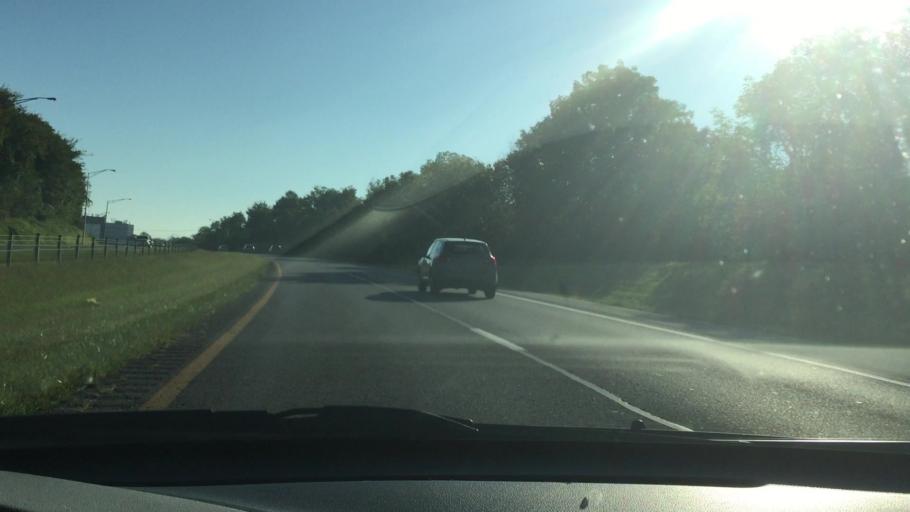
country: US
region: Kentucky
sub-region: Fayette County
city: Lexington
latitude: 37.9927
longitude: -84.4730
